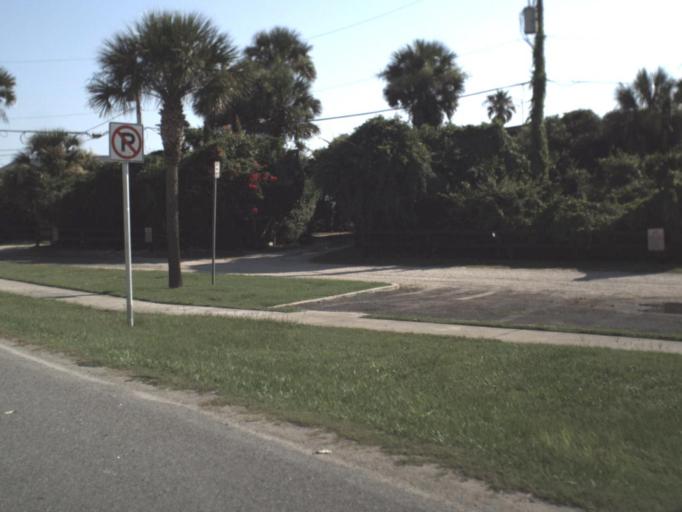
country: US
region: Florida
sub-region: Saint Johns County
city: Butler Beach
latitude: 29.7027
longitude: -81.2273
